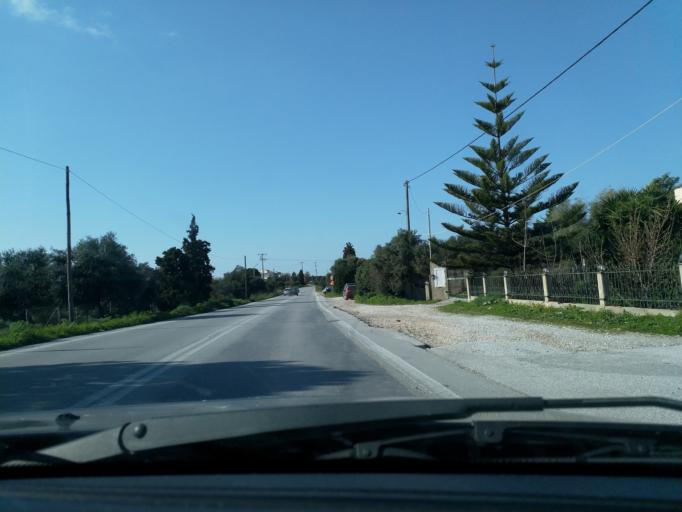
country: GR
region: Crete
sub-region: Nomos Chanias
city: Pithari
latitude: 35.5176
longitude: 24.0726
